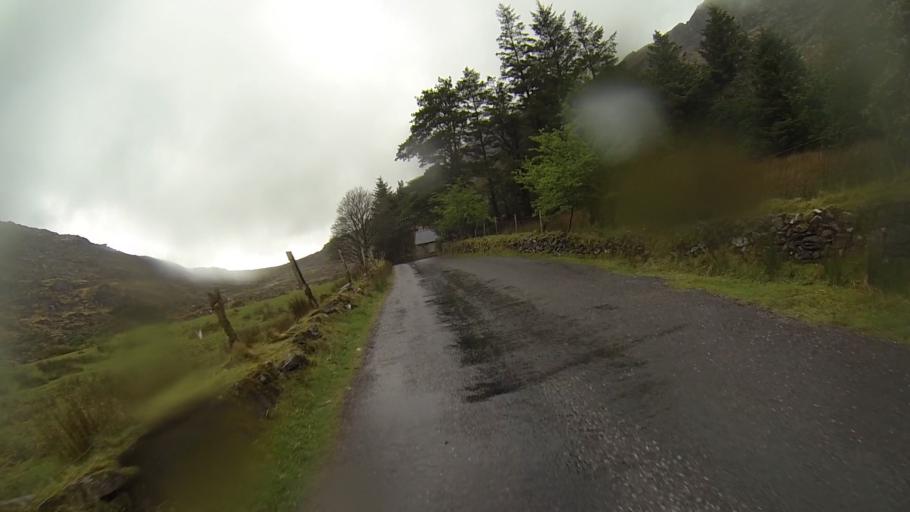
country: IE
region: Munster
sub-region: Ciarrai
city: Kenmare
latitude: 52.0001
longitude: -9.6446
